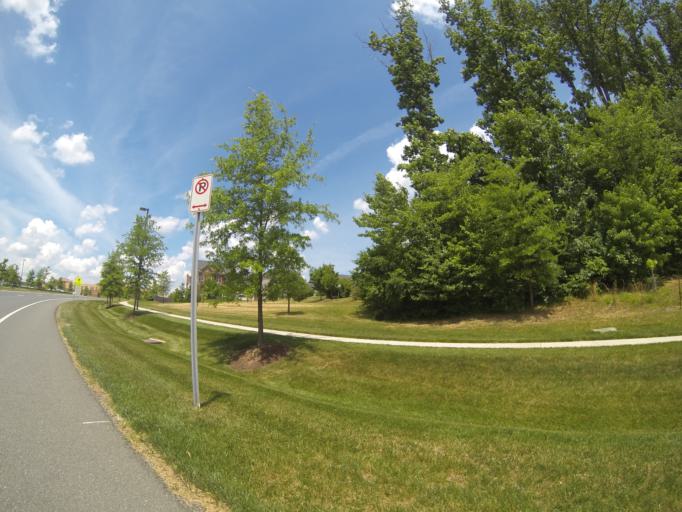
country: US
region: Maryland
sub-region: Montgomery County
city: Clarksburg
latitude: 39.2344
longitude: -77.2608
